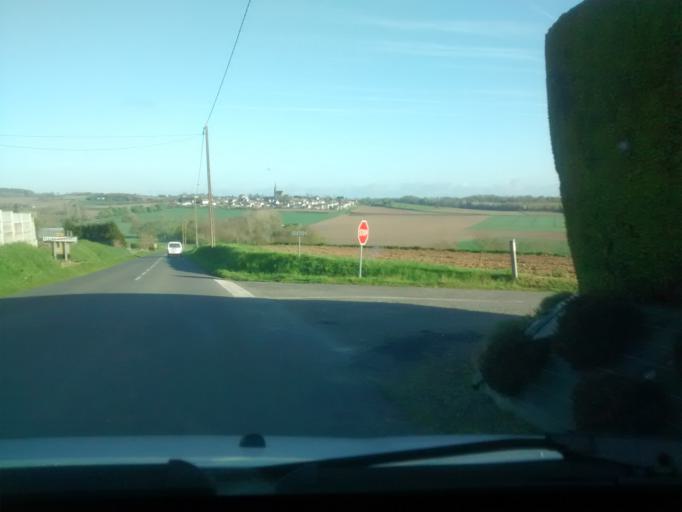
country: FR
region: Brittany
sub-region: Departement d'Ille-et-Vilaine
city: Pleine-Fougeres
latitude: 48.5413
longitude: -1.5708
